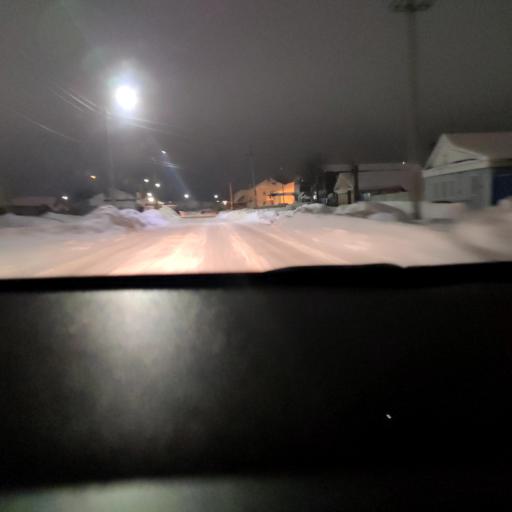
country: RU
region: Tatarstan
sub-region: Chistopol'skiy Rayon
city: Chistopol'
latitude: 55.3591
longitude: 50.6289
